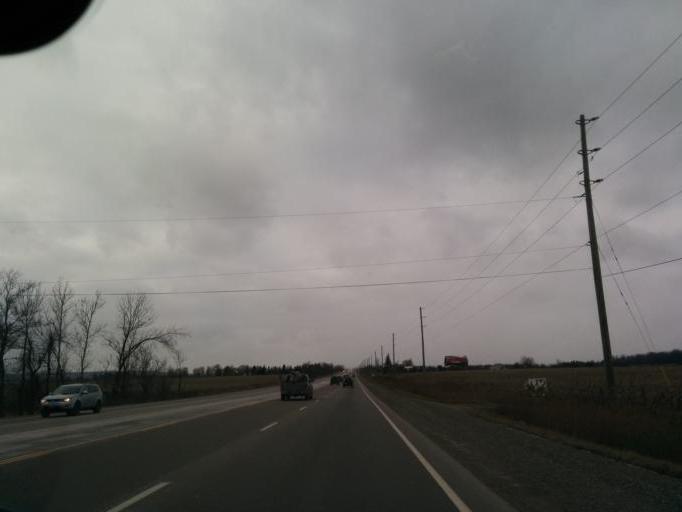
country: CA
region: Ontario
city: Brampton
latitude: 43.7583
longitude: -79.8577
